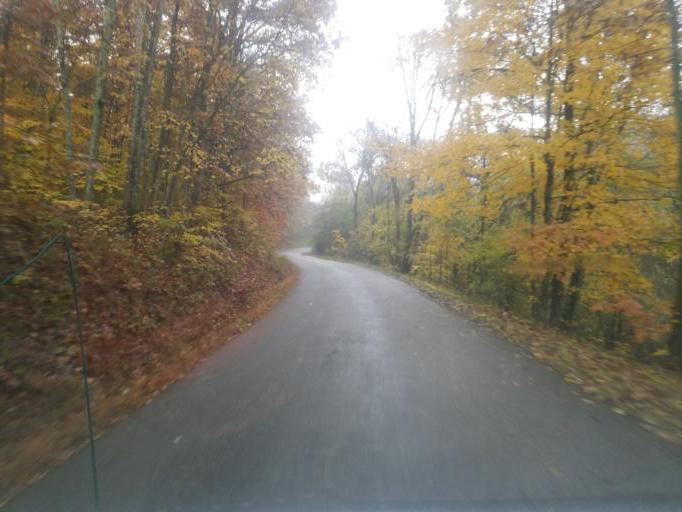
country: US
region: Ohio
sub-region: Athens County
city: Glouster
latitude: 39.5254
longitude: -81.9490
